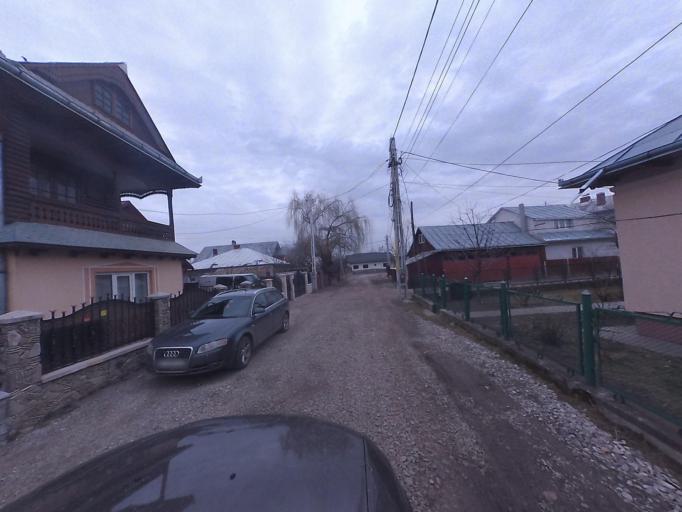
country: RO
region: Neamt
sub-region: Oras Targu Neamt
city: Targu Neamt
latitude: 47.2084
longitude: 26.3778
